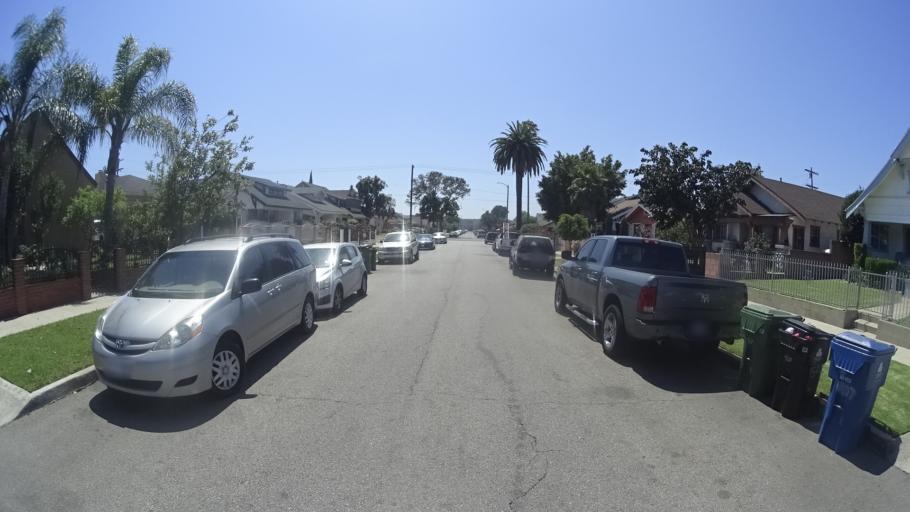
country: US
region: California
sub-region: Los Angeles County
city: View Park-Windsor Hills
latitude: 34.0010
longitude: -118.3036
